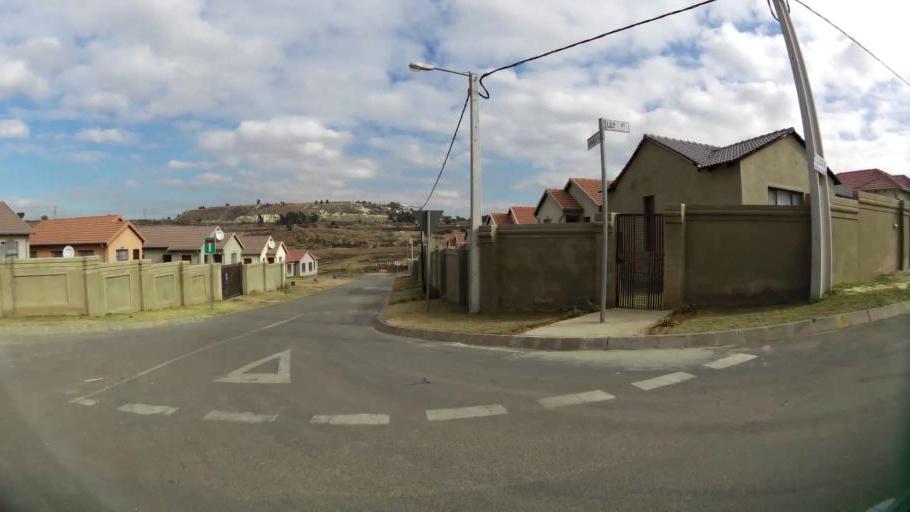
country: ZA
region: Gauteng
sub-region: City of Johannesburg Metropolitan Municipality
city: Roodepoort
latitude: -26.2049
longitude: 27.9096
